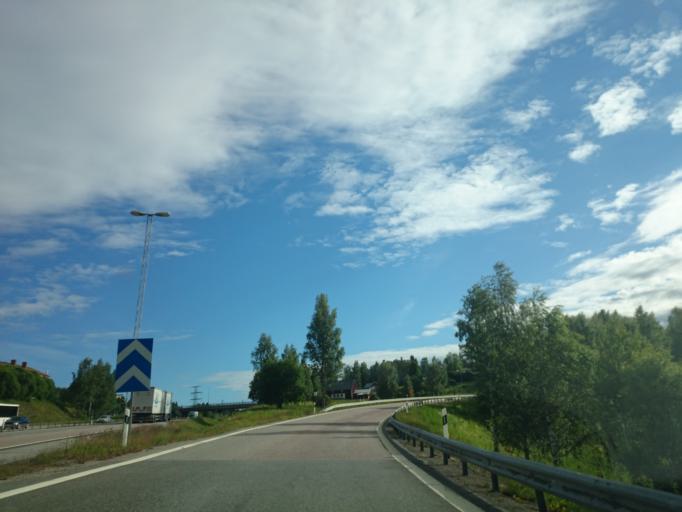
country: SE
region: Vaesternorrland
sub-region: Timra Kommun
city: Timra
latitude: 62.4777
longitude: 17.3128
